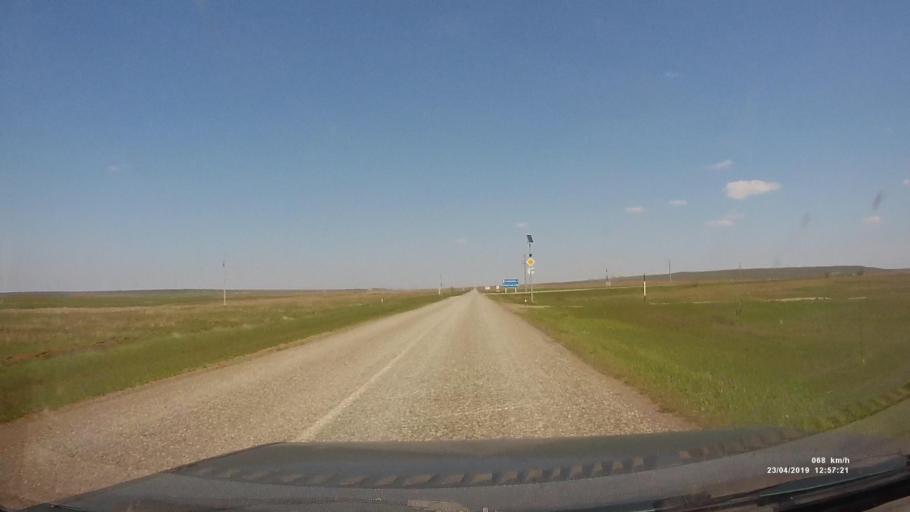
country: RU
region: Kalmykiya
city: Yashalta
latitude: 46.6030
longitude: 42.5804
